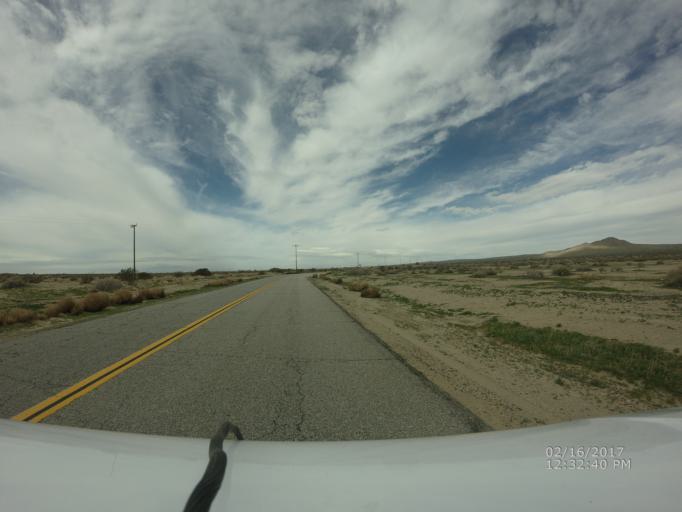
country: US
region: California
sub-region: Los Angeles County
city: Lake Los Angeles
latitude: 34.6687
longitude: -117.8448
